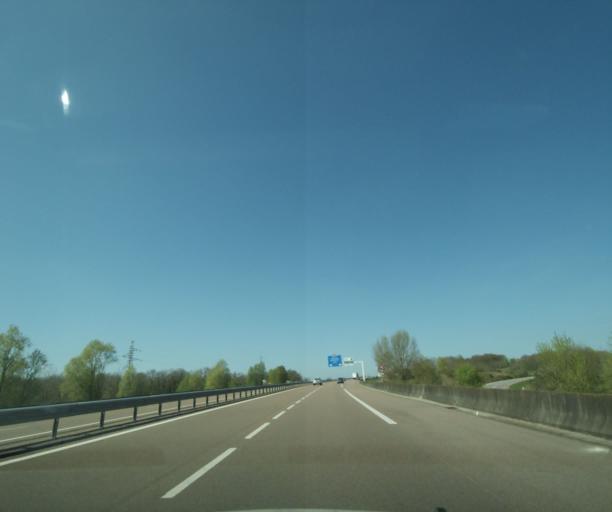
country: FR
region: Bourgogne
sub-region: Departement de la Nievre
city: Cosne-Cours-sur-Loire
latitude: 47.4275
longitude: 2.9405
